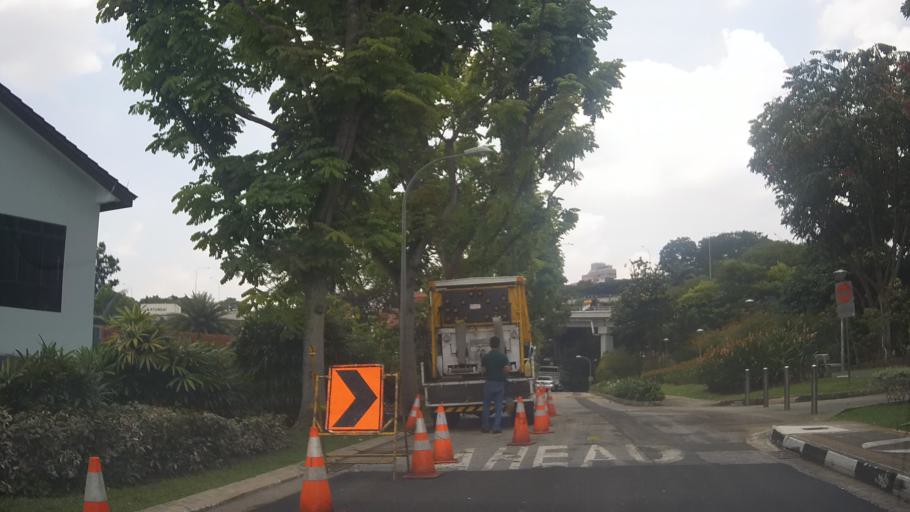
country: SG
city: Singapore
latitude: 1.3409
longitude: 103.7809
